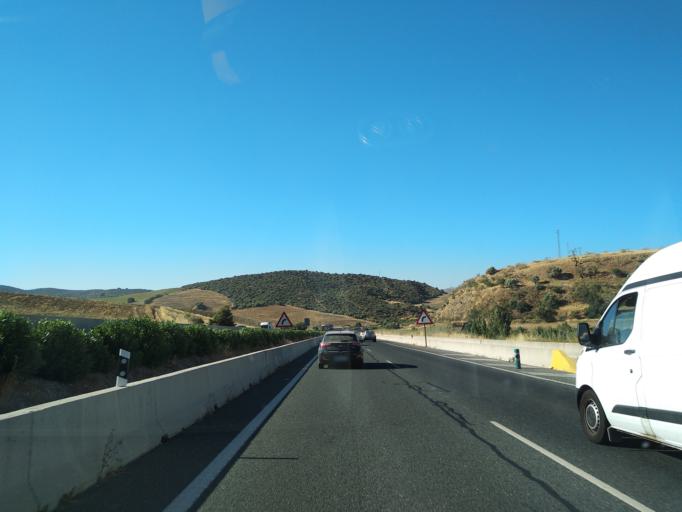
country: ES
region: Andalusia
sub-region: Provincia de Malaga
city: Casabermeja
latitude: 36.9422
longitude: -4.4399
